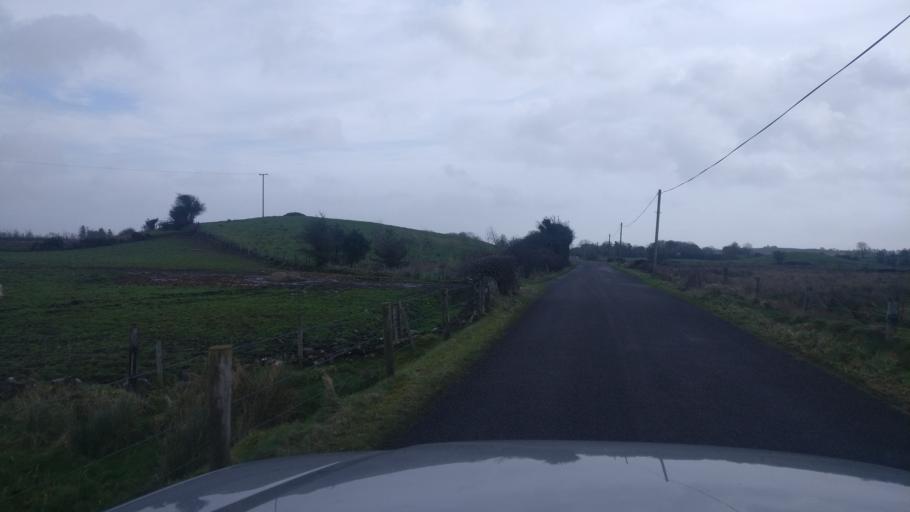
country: IE
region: Connaught
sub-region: County Galway
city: Loughrea
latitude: 53.2822
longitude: -8.4551
